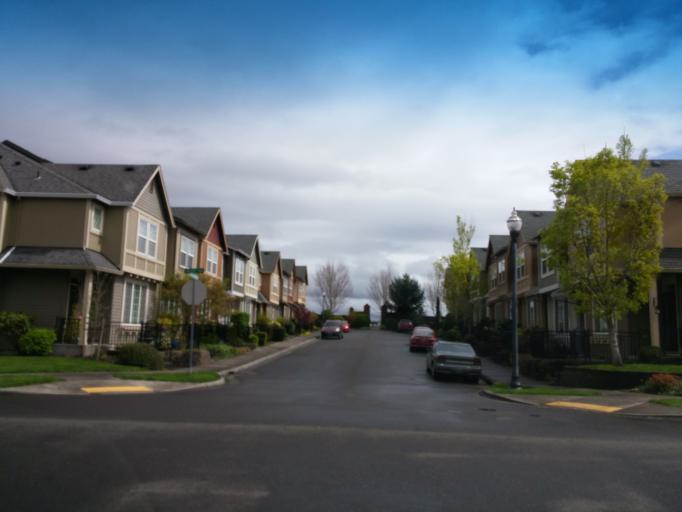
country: US
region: Oregon
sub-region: Washington County
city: Aloha
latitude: 45.5070
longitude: -122.8532
